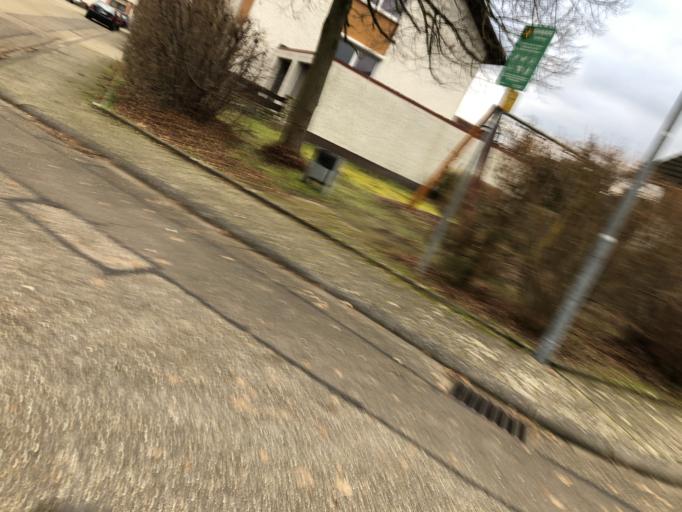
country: DE
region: Baden-Wuerttemberg
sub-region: Karlsruhe Region
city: Altlussheim
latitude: 49.3002
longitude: 8.5033
